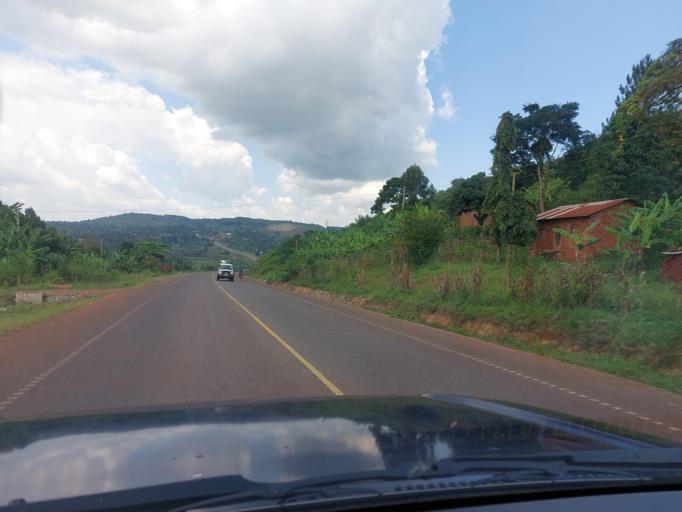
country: UG
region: Central Region
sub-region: Buikwe District
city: Njeru
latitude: 0.3363
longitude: 33.1242
